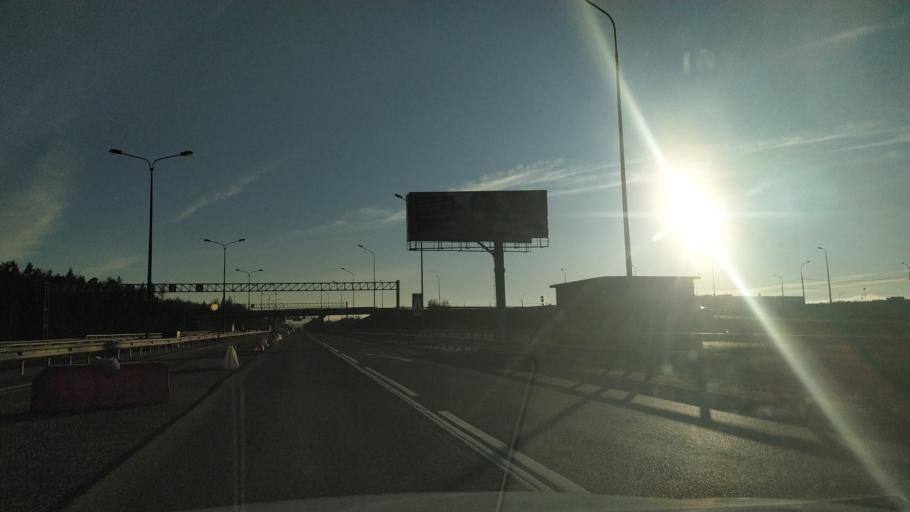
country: RU
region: St.-Petersburg
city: Ol'gino
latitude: 60.0570
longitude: 30.1308
